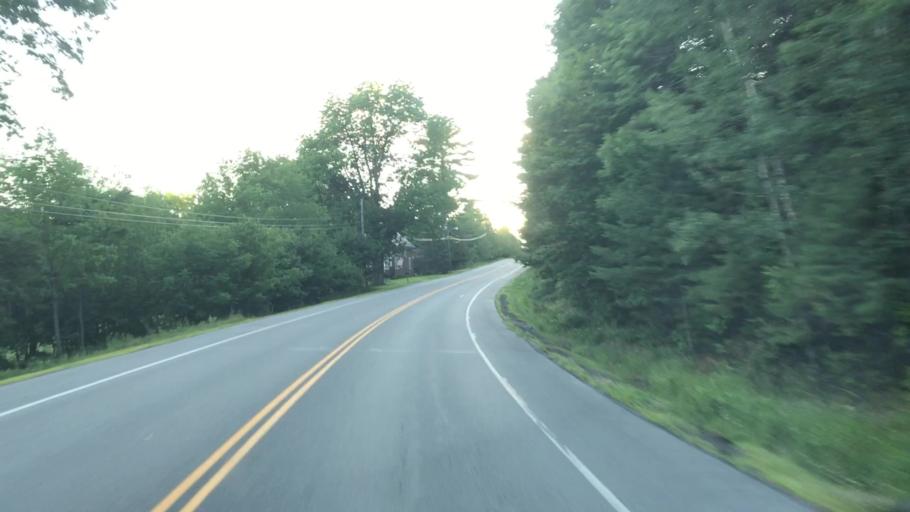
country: US
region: Maine
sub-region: Penobscot County
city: Lincoln
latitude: 45.3738
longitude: -68.4727
